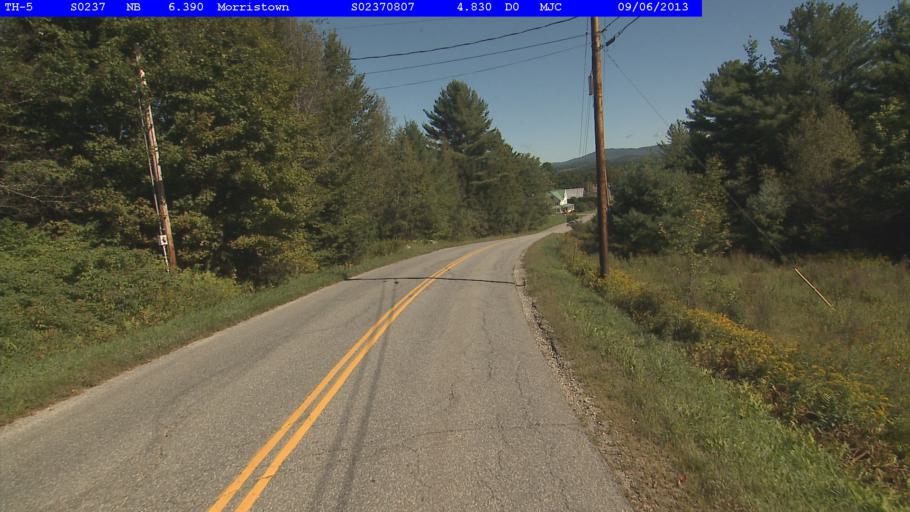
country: US
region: Vermont
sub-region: Lamoille County
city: Morristown
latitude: 44.5651
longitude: -72.6210
